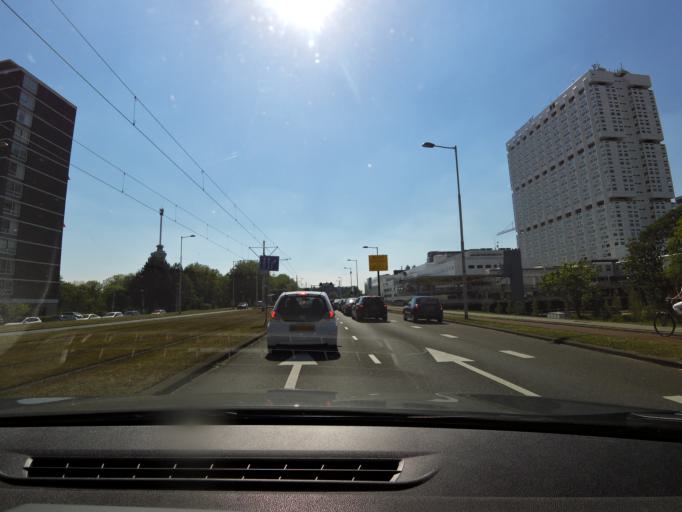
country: NL
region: South Holland
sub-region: Gemeente Rotterdam
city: Rotterdam
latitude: 51.9100
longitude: 4.4726
